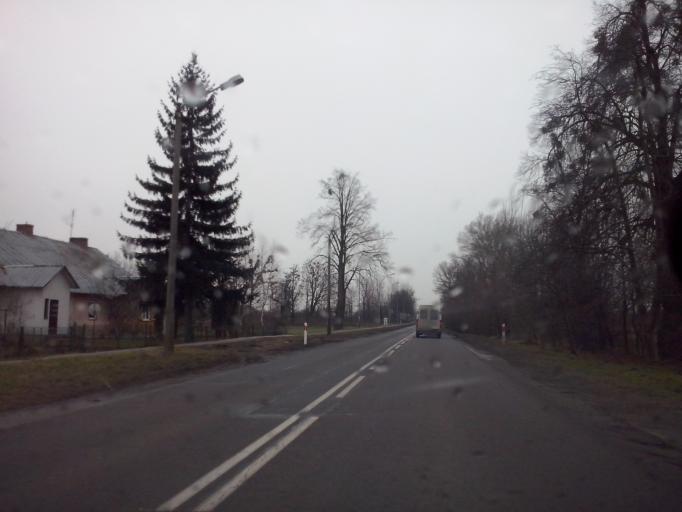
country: PL
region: Lublin Voivodeship
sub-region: Powiat zamojski
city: Michalow
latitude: 50.7131
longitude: 23.0073
